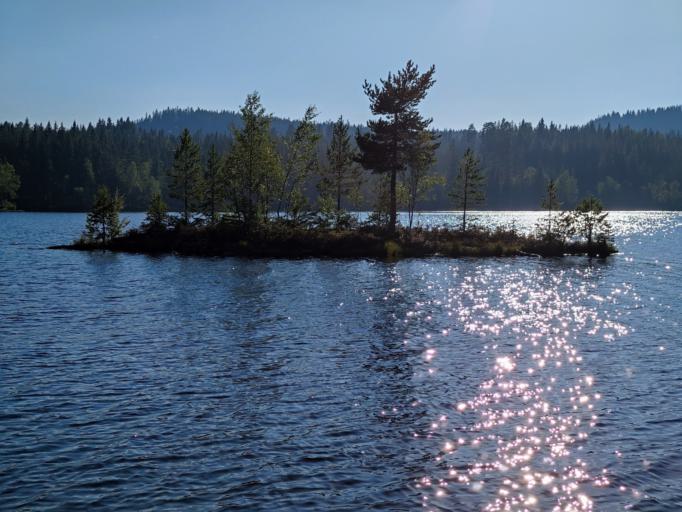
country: NO
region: Akershus
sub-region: Nittedal
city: Rotnes
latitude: 60.0762
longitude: 10.8163
